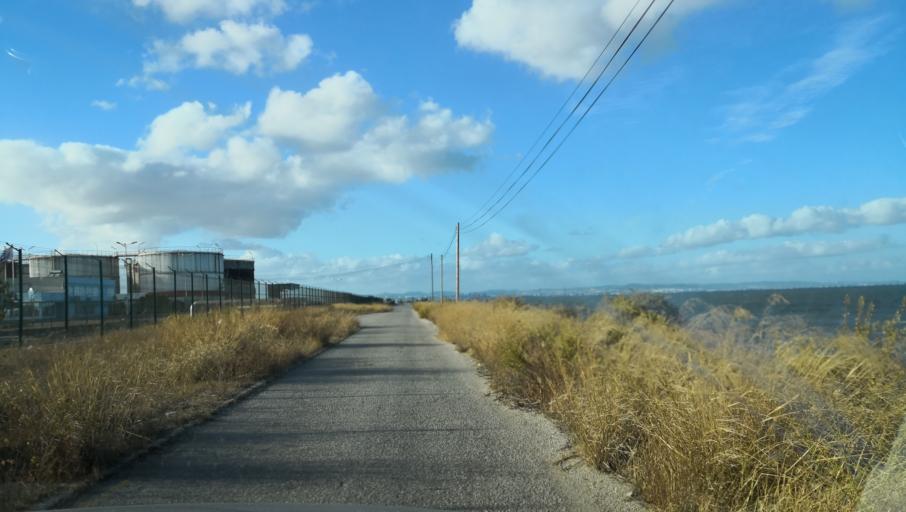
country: PT
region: Setubal
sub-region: Barreiro
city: Barreiro
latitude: 38.6809
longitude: -9.0565
